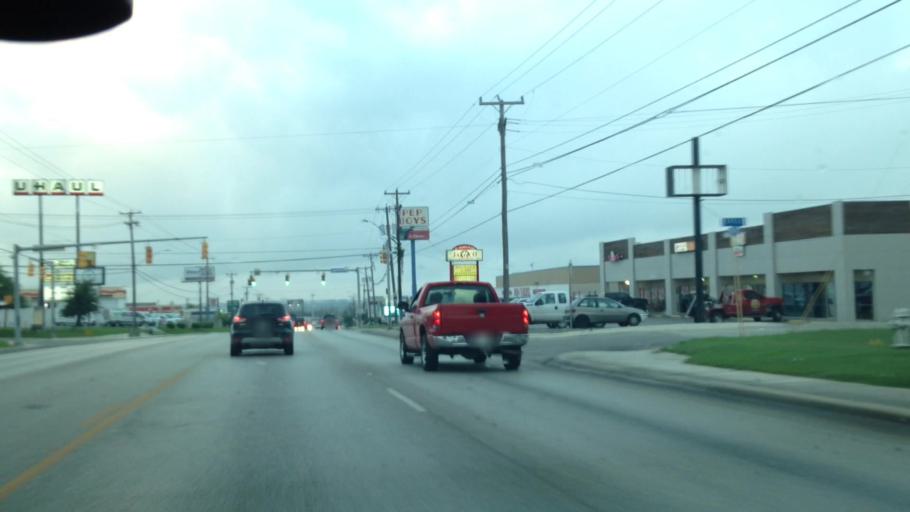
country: US
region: Texas
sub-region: Bexar County
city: Windcrest
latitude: 29.5551
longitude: -98.4014
